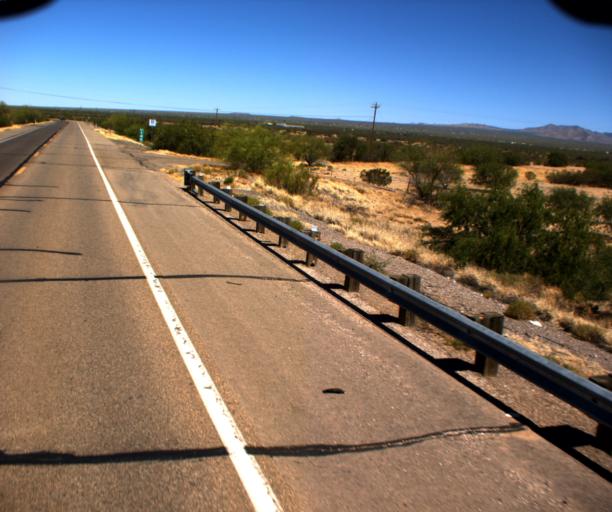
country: US
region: Arizona
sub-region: Pima County
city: Three Points
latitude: 32.0755
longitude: -111.3383
